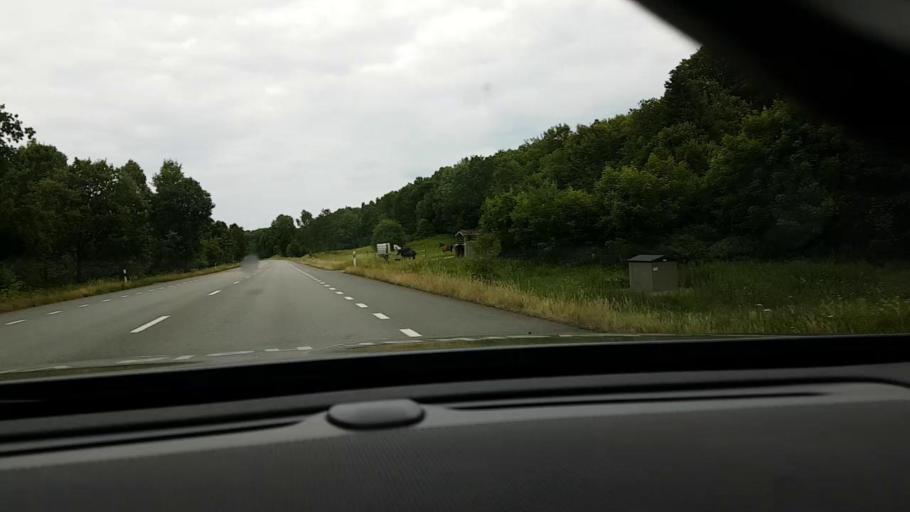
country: SE
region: Skane
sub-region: Hassleholms Kommun
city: Tormestorp
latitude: 56.0961
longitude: 13.7735
